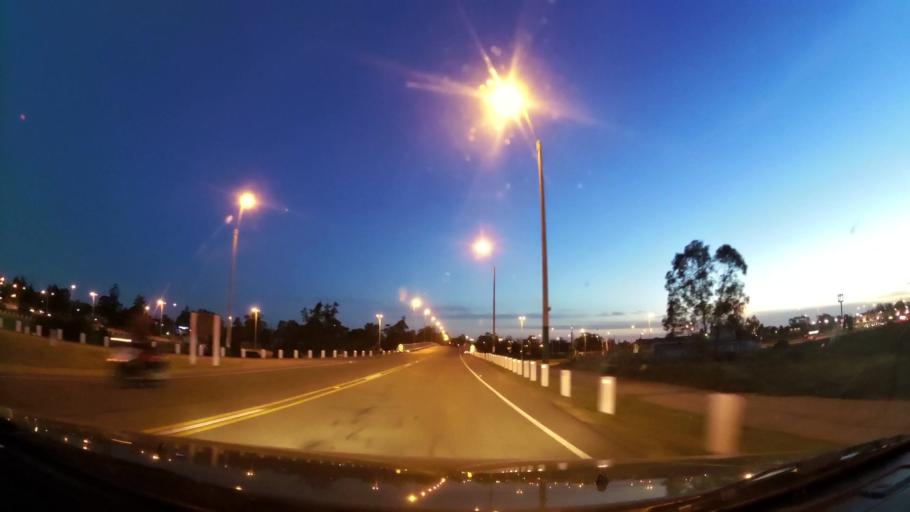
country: UY
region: Canelones
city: Atlantida
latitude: -34.7655
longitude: -55.7646
